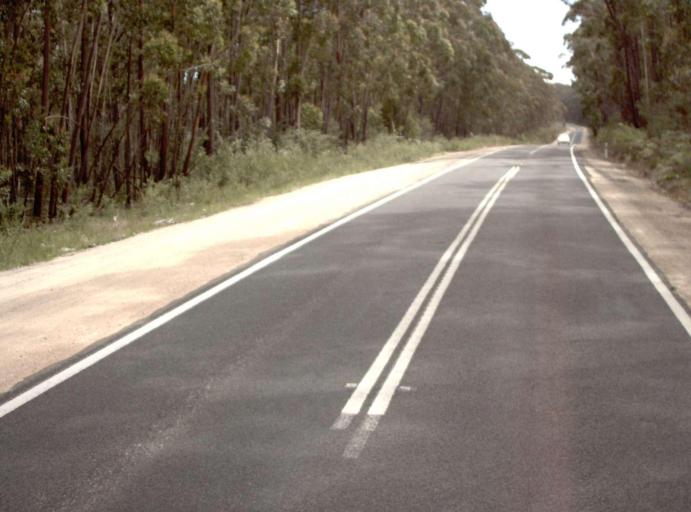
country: AU
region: New South Wales
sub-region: Bega Valley
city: Eden
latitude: -37.4988
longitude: 149.5440
